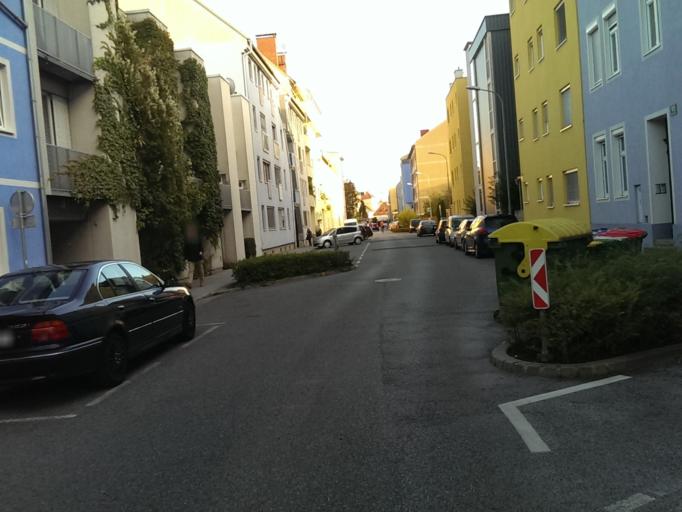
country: AT
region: Styria
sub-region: Graz Stadt
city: Graz
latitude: 47.0820
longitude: 15.4268
